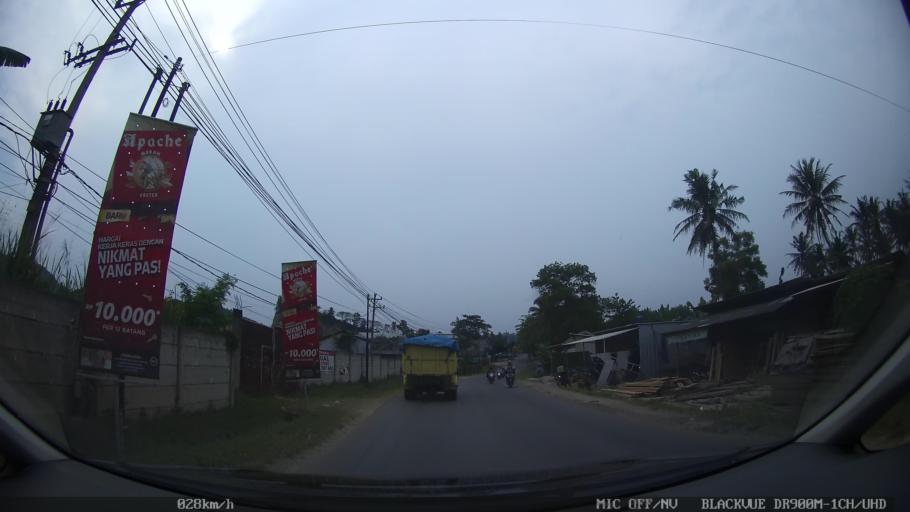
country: ID
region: Lampung
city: Panjang
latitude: -5.4136
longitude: 105.3223
